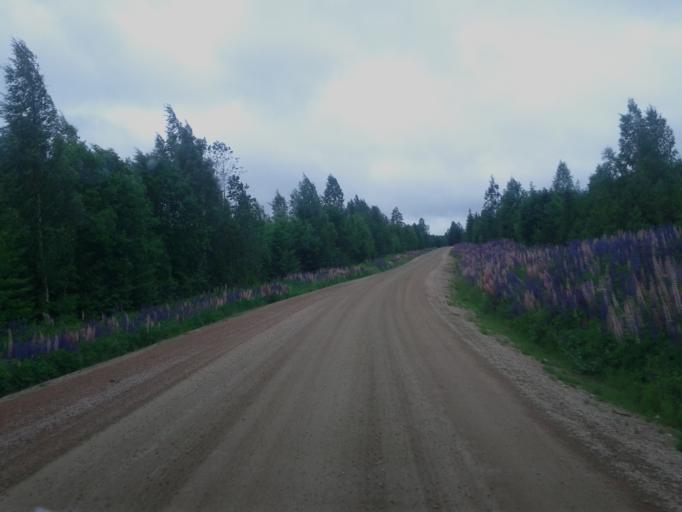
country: SE
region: Gaevleborg
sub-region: Hudiksvalls Kommun
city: Delsbo
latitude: 62.1305
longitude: 16.6504
